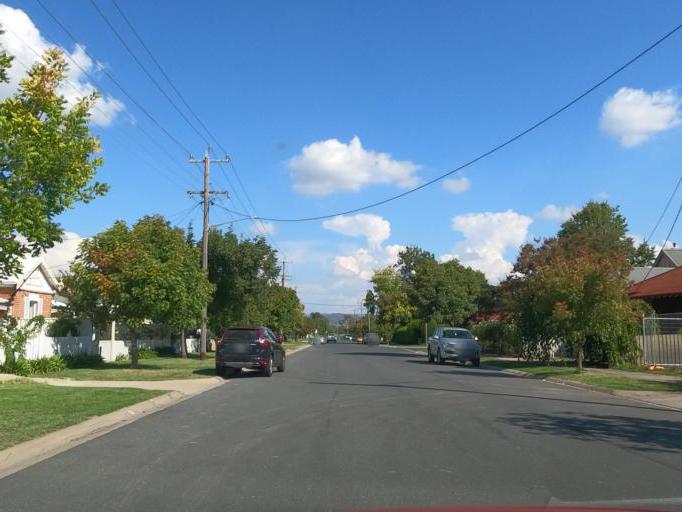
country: AU
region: New South Wales
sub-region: Albury Municipality
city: South Albury
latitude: -36.0892
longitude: 146.9207
